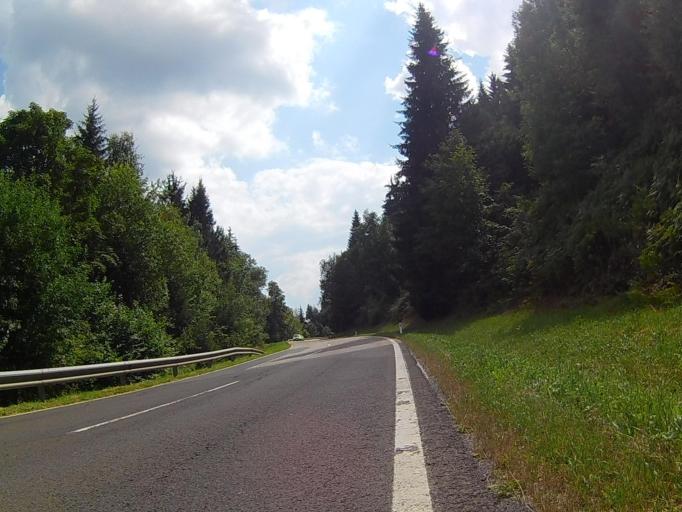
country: AT
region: Styria
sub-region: Politischer Bezirk Deutschlandsberg
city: Soboth
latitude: 46.6930
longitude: 15.1022
